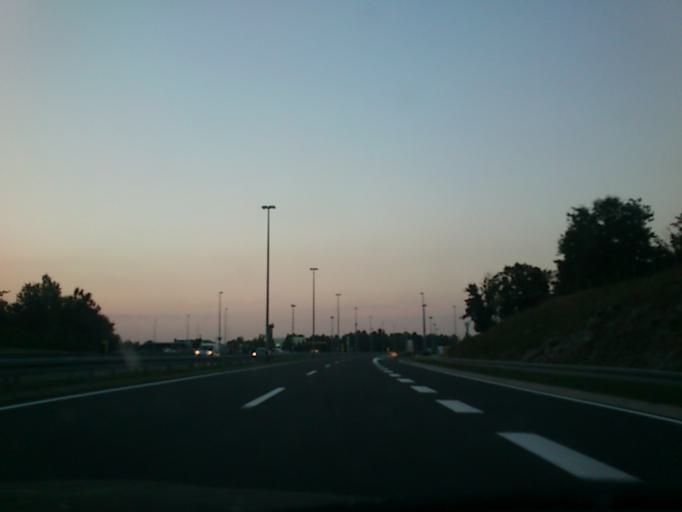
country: HR
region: Karlovacka
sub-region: Grad Ogulin
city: Ogulin
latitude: 45.3060
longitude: 15.2791
